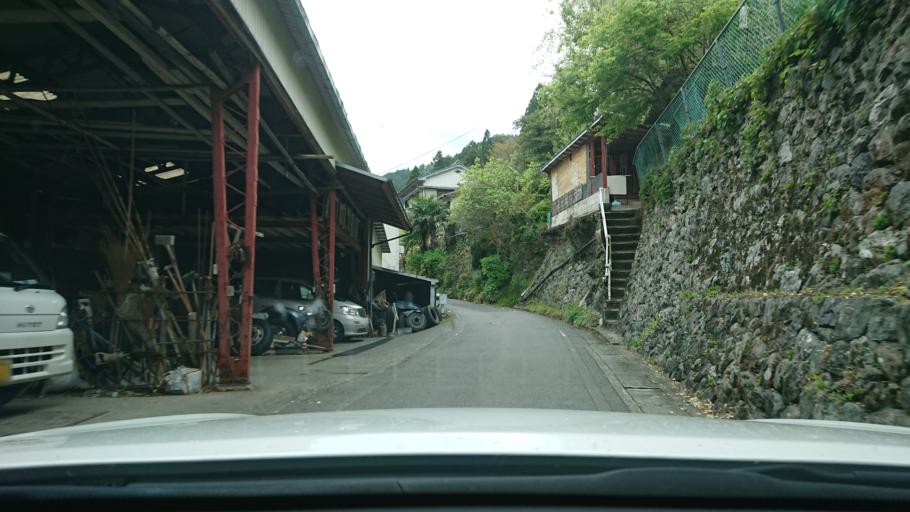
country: JP
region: Tokushima
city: Ishii
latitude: 33.8878
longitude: 134.4008
